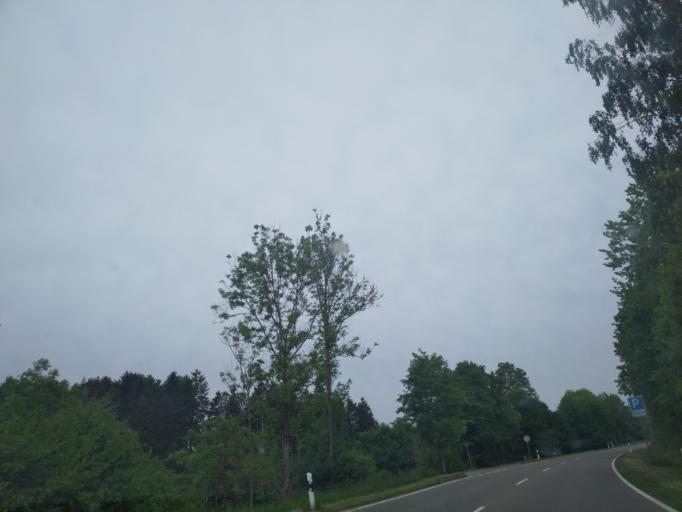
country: DE
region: Baden-Wuerttemberg
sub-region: Freiburg Region
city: Bonndorf im Schwarzwald
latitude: 47.8022
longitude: 8.3467
